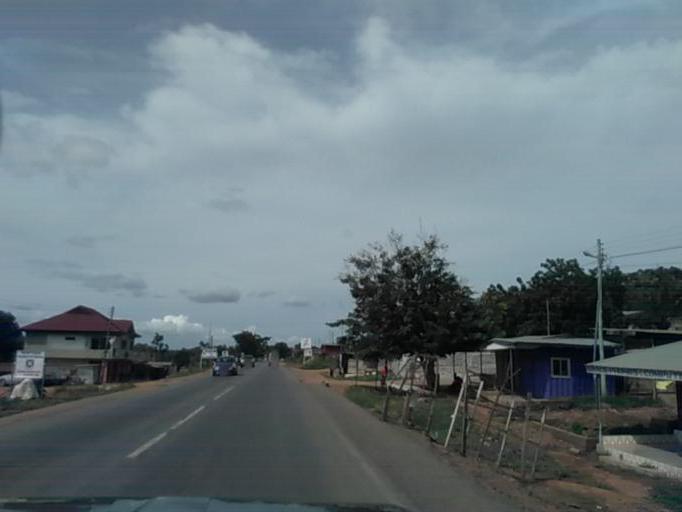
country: GH
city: Akropong
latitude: 6.2253
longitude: 0.0876
